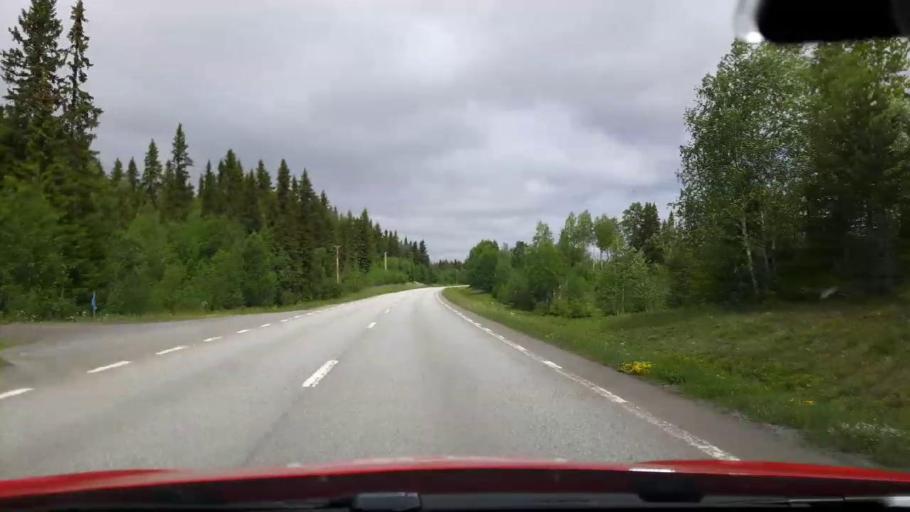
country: SE
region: Jaemtland
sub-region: Krokoms Kommun
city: Krokom
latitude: 63.4935
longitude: 14.5076
